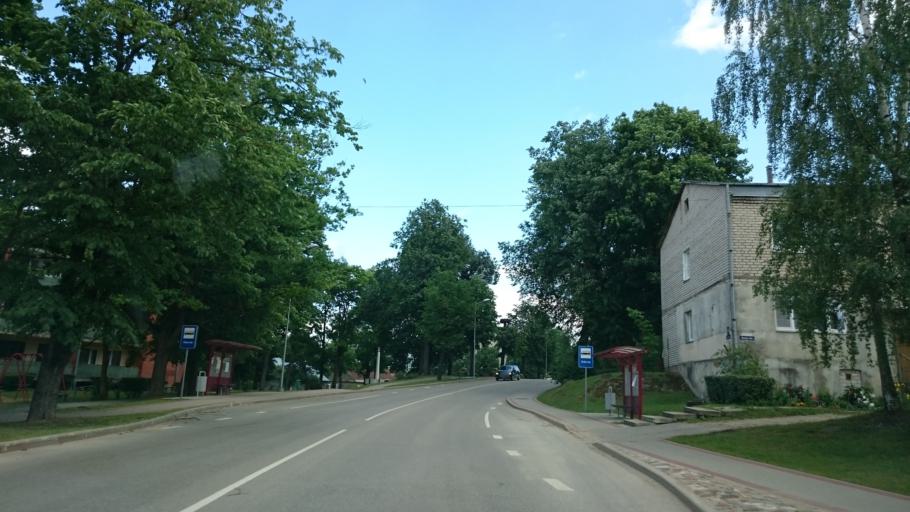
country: LV
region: Ludzas Rajons
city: Ludza
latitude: 56.5465
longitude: 27.7177
